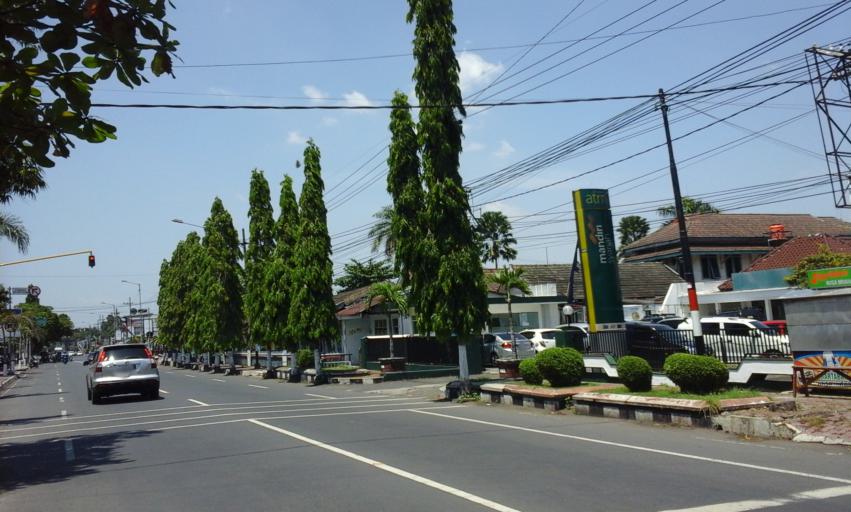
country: ID
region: East Java
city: Krajan
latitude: -8.1648
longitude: 113.7058
